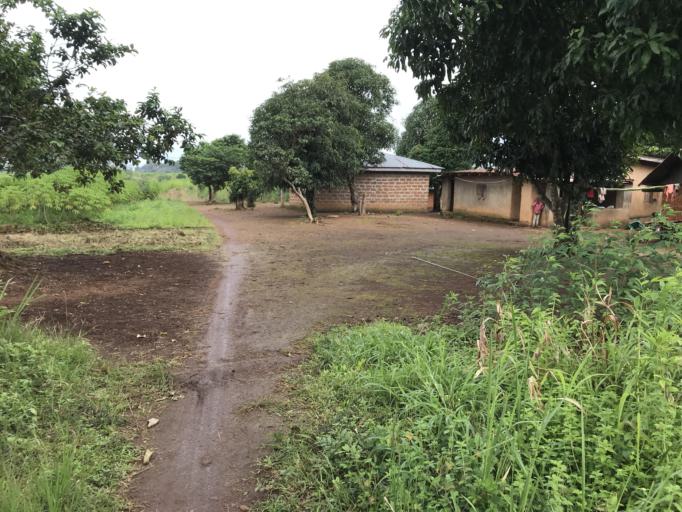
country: SL
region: Eastern Province
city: Buedu
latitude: 8.4726
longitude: -10.3152
